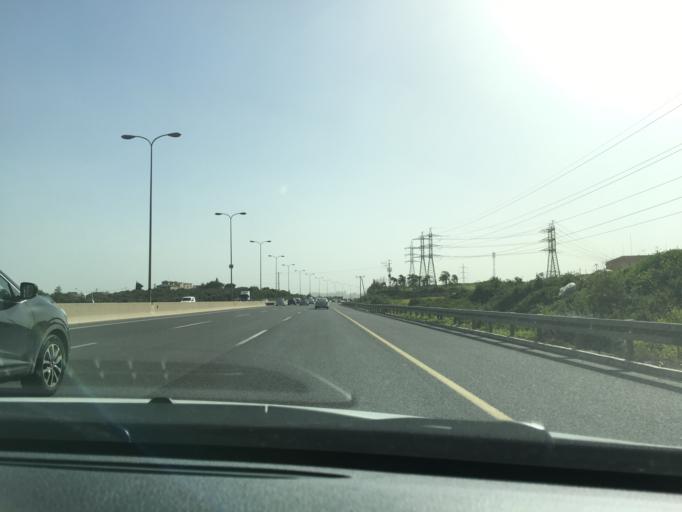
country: IL
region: Central District
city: Hod HaSharon
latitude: 32.1490
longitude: 34.8732
